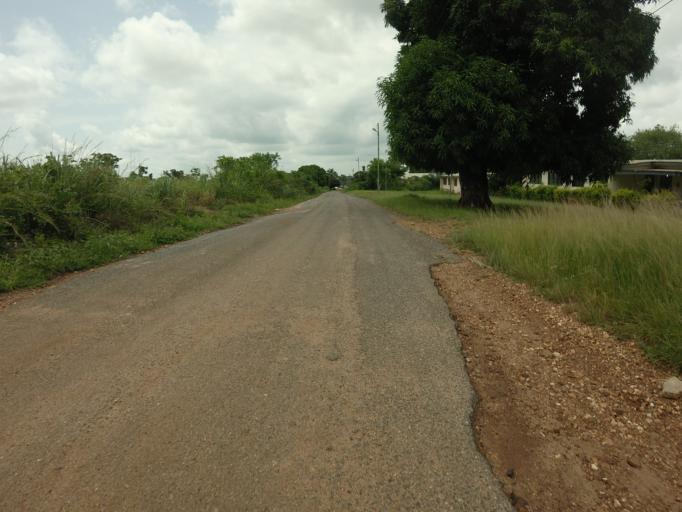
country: GH
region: Volta
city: Ho
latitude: 6.5982
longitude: 0.4809
